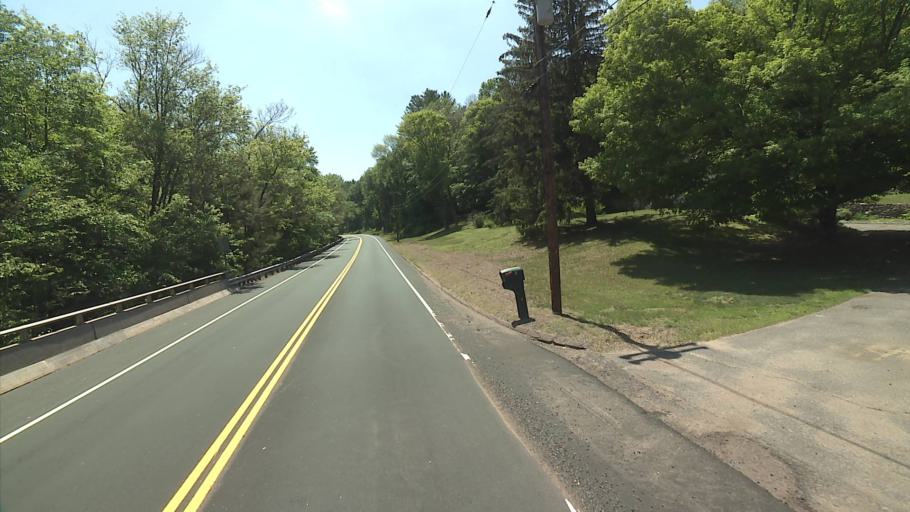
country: US
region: Connecticut
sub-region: Tolland County
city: Crystal Lake
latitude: 41.9651
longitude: -72.3631
